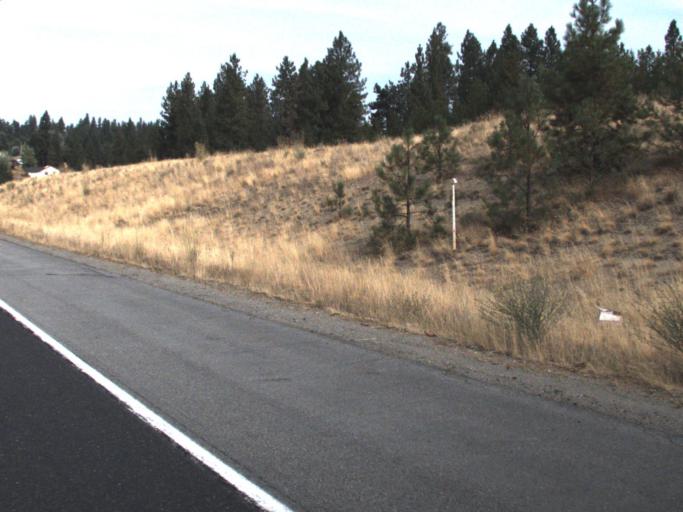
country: US
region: Washington
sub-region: Spokane County
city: Fairwood
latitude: 47.8173
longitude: -117.4104
